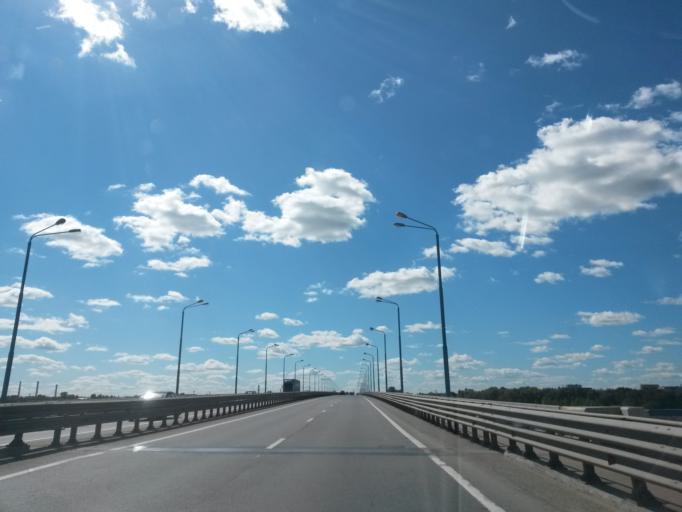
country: RU
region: Jaroslavl
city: Yaroslavl
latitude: 57.6760
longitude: 39.8600
